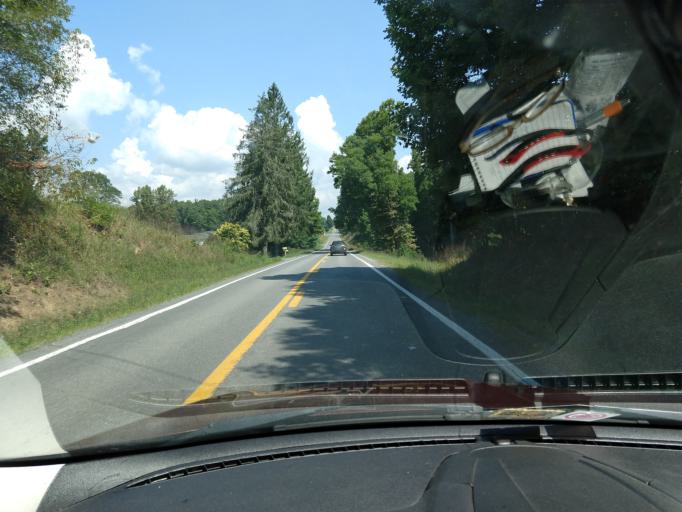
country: US
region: West Virginia
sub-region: Greenbrier County
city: Fairlea
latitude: 37.8376
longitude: -80.5546
